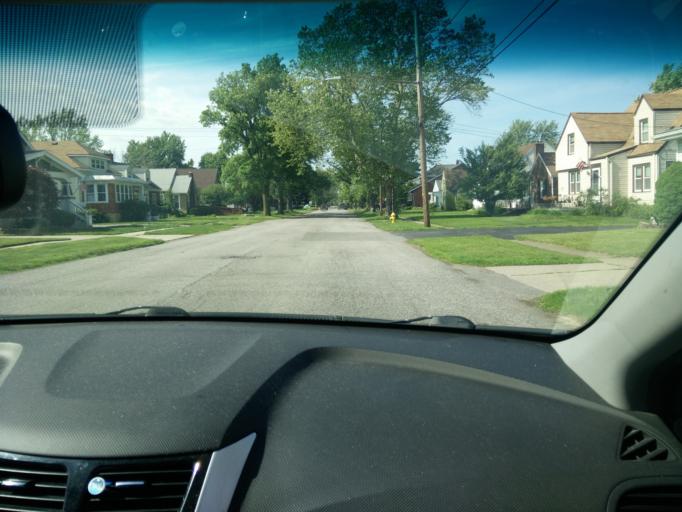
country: US
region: New York
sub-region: Erie County
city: West Seneca
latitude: 42.8351
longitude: -78.7974
